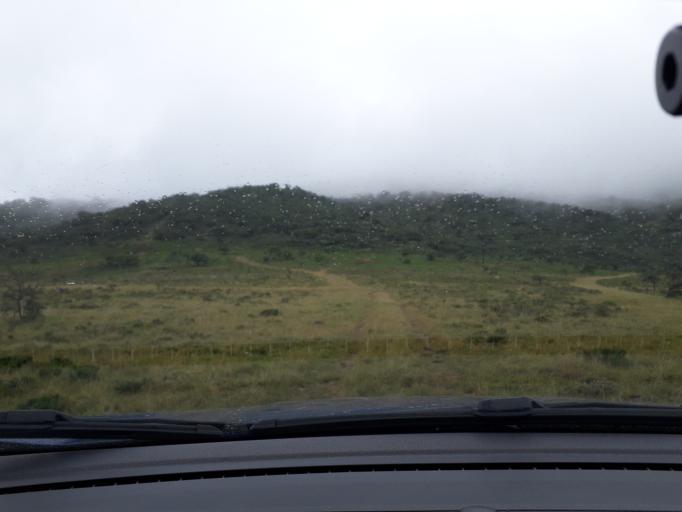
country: ZA
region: Eastern Cape
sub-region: Buffalo City Metropolitan Municipality
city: Bhisho
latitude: -32.7302
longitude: 27.3711
